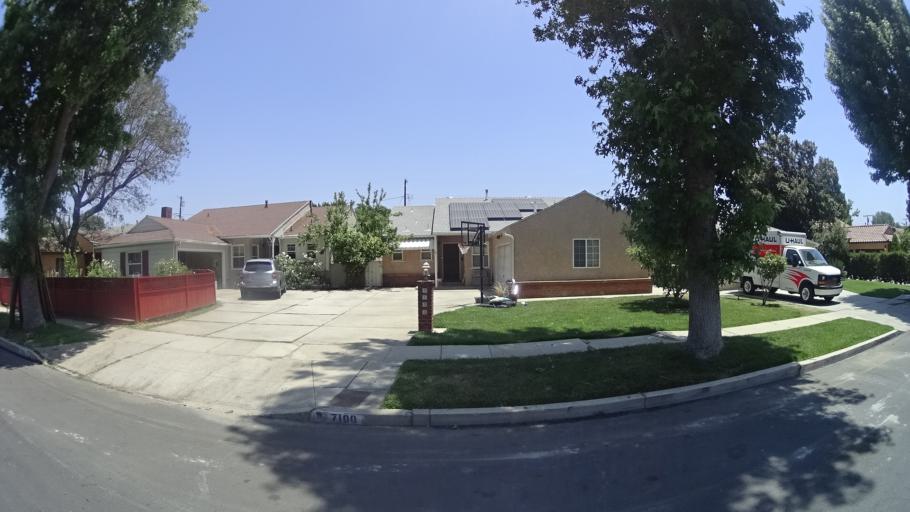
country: US
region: California
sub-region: Los Angeles County
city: Van Nuys
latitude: 34.1997
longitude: -118.4335
